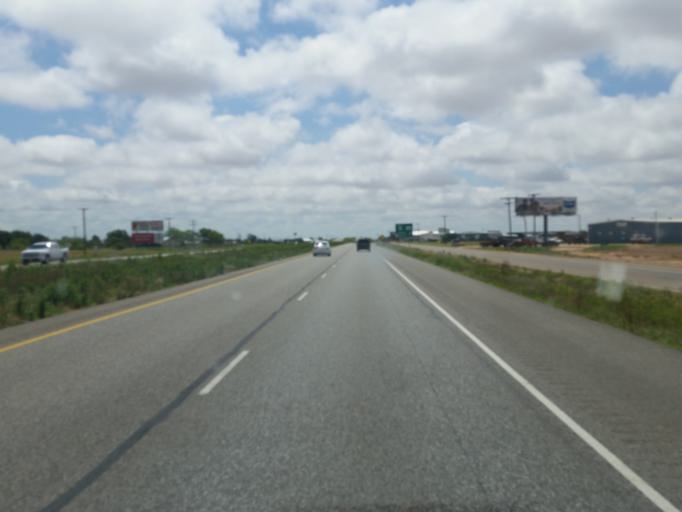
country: US
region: Texas
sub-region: Lubbock County
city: Slaton
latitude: 33.4251
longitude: -101.6519
